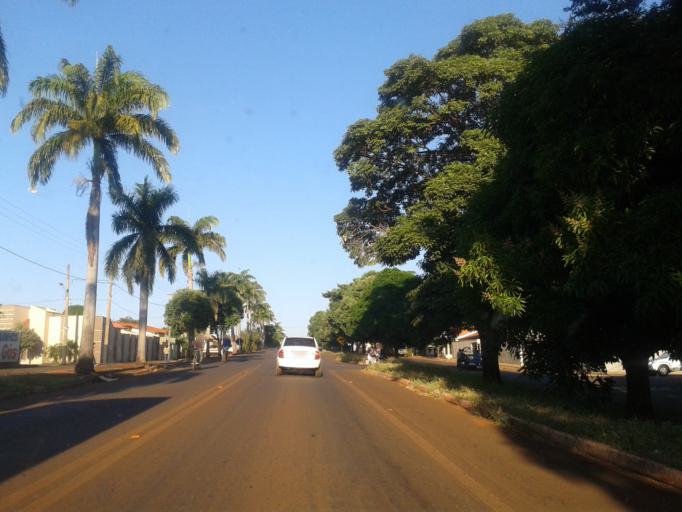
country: BR
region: Minas Gerais
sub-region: Capinopolis
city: Capinopolis
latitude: -18.6884
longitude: -49.5676
